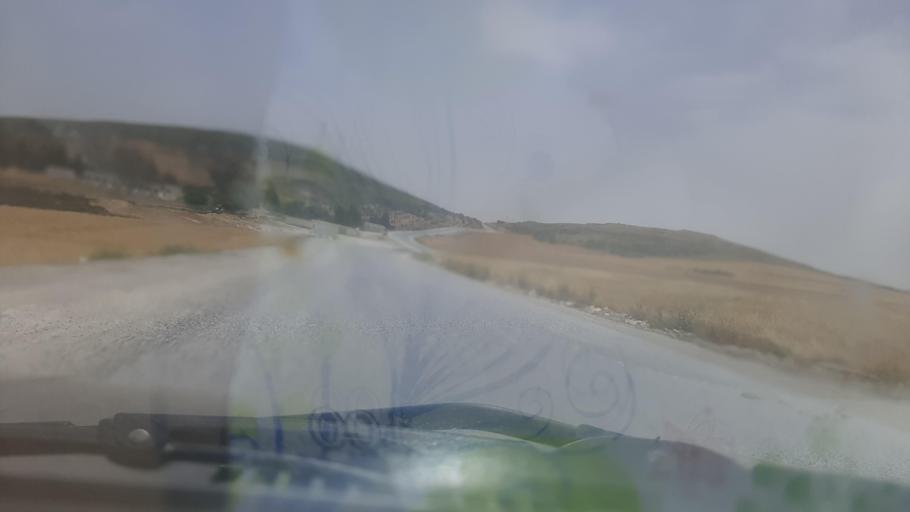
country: TN
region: Tunis
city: La Mohammedia
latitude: 36.5389
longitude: 10.1525
